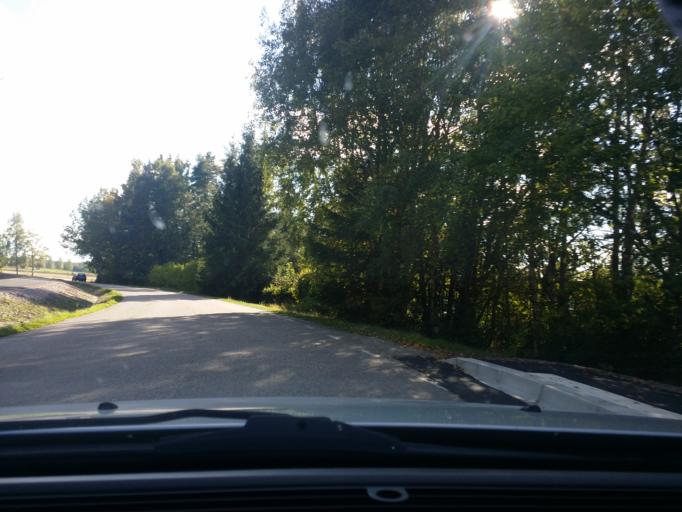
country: SE
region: Vaestmanland
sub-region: Vasteras
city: Vasteras
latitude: 59.5776
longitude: 16.4896
